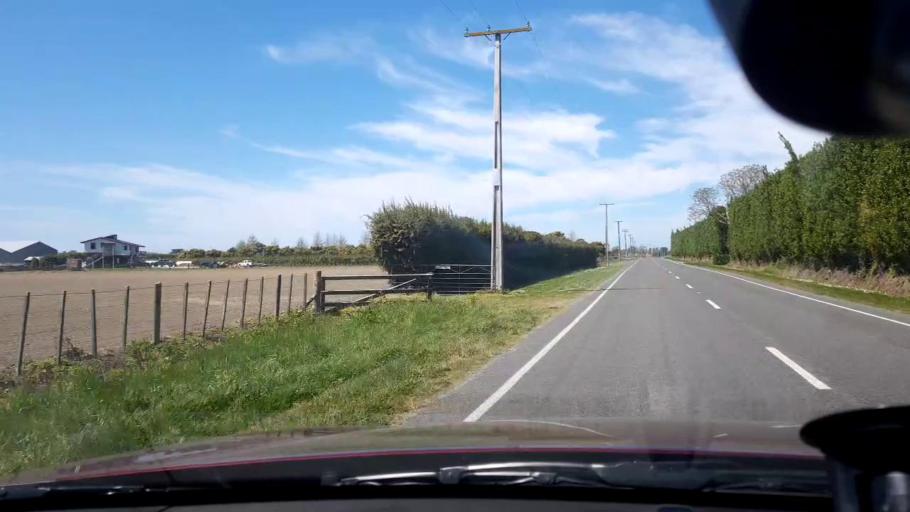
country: NZ
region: Gisborne
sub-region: Gisborne District
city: Gisborne
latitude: -38.6275
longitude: 177.9250
